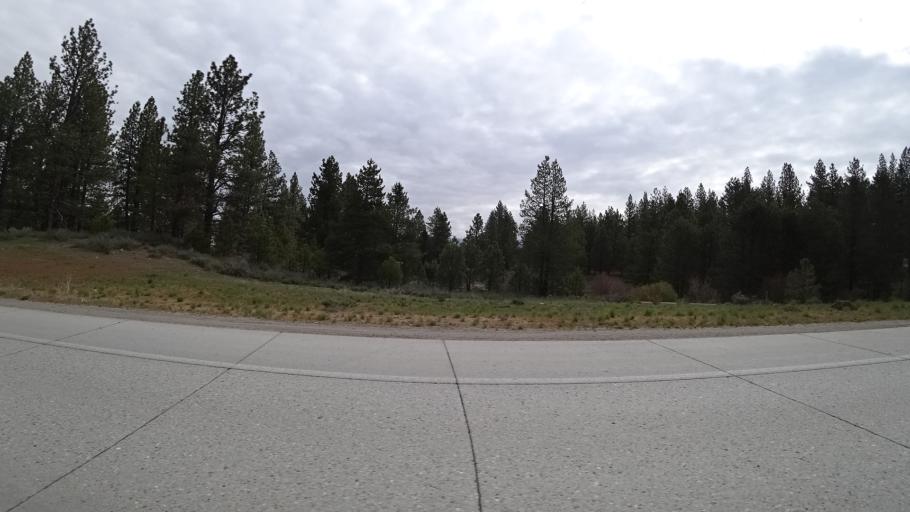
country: US
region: California
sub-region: Nevada County
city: Truckee
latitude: 39.3281
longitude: -120.1590
